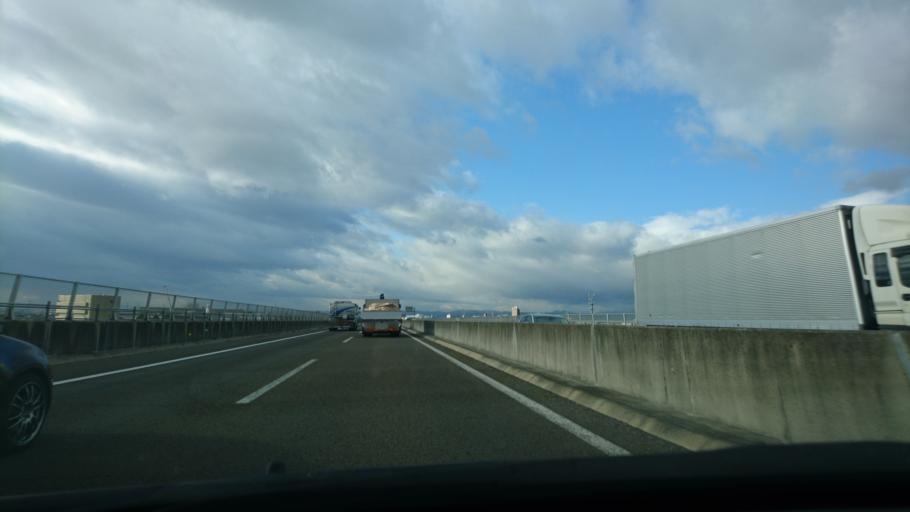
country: JP
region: Miyagi
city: Rifu
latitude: 38.2635
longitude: 140.9710
